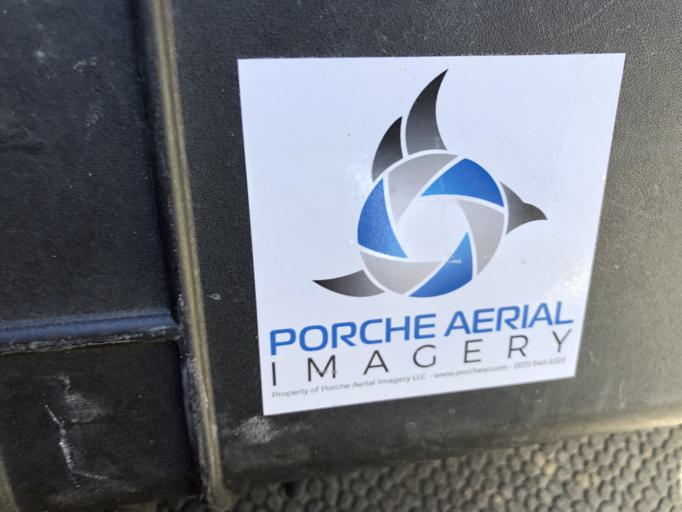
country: US
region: Louisiana
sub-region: Calcasieu Parish
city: Iowa
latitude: 30.3188
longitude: -93.0788
